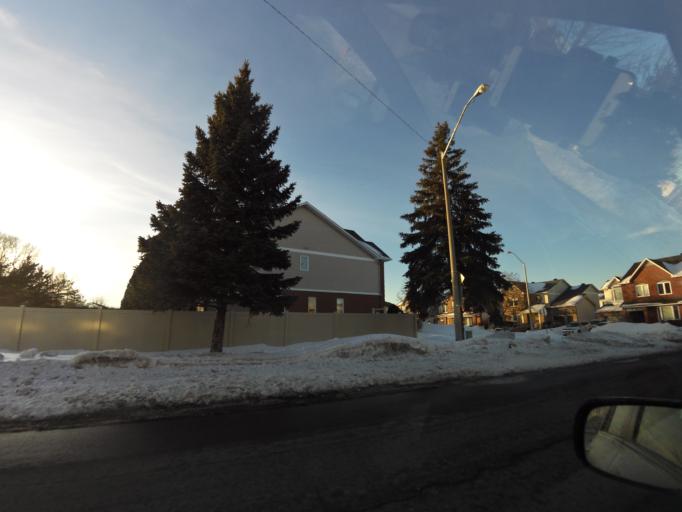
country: CA
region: Ontario
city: Ottawa
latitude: 45.4409
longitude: -75.5313
